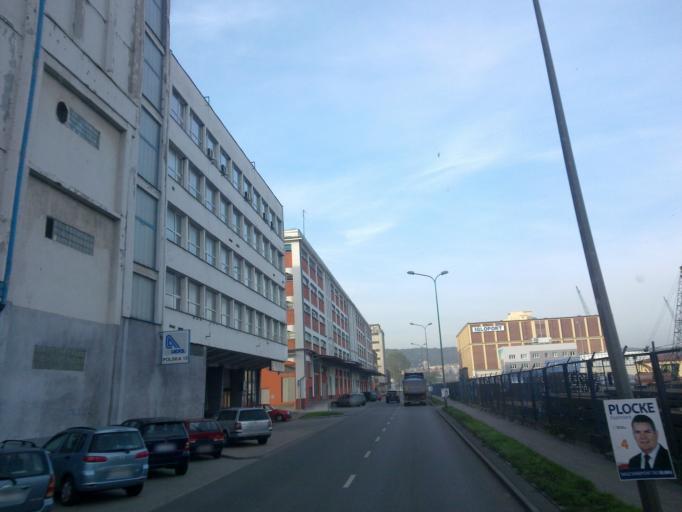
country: PL
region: Pomeranian Voivodeship
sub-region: Gdynia
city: Gdynia
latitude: 54.5292
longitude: 18.5354
